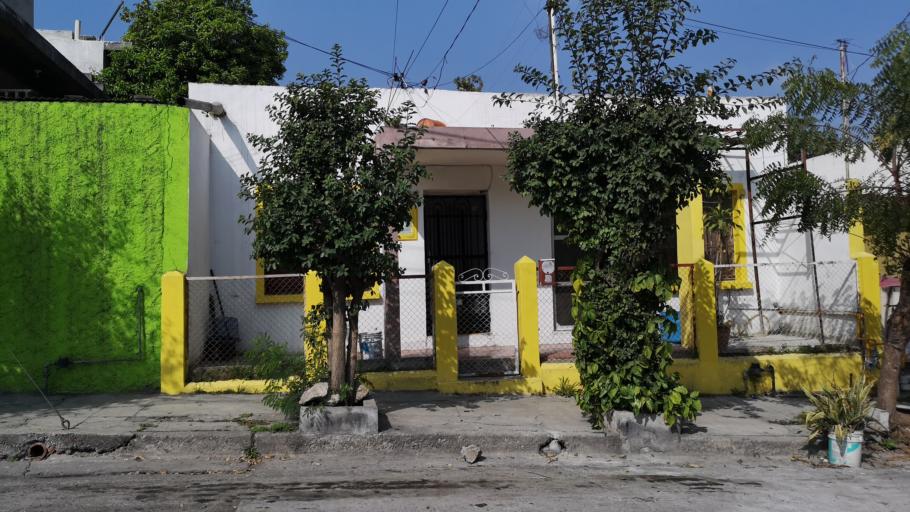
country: MX
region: Nuevo Leon
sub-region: Monterrey
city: Monterrey
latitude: 25.6552
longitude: -100.3155
